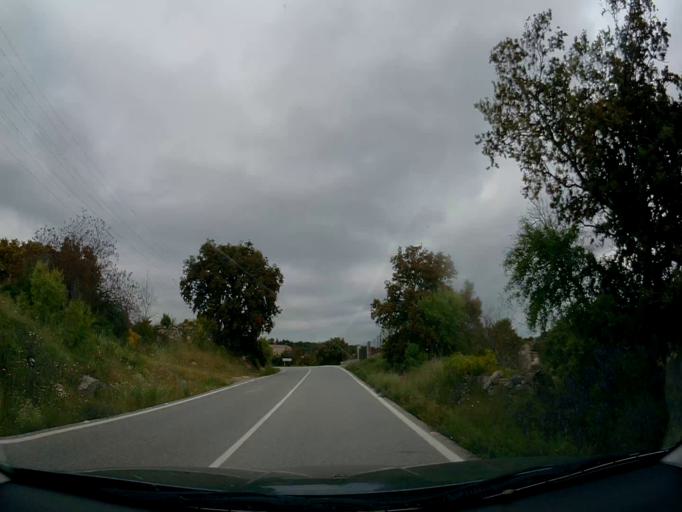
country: ES
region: Madrid
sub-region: Provincia de Madrid
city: Navalagamella
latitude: 40.4647
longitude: -4.1182
